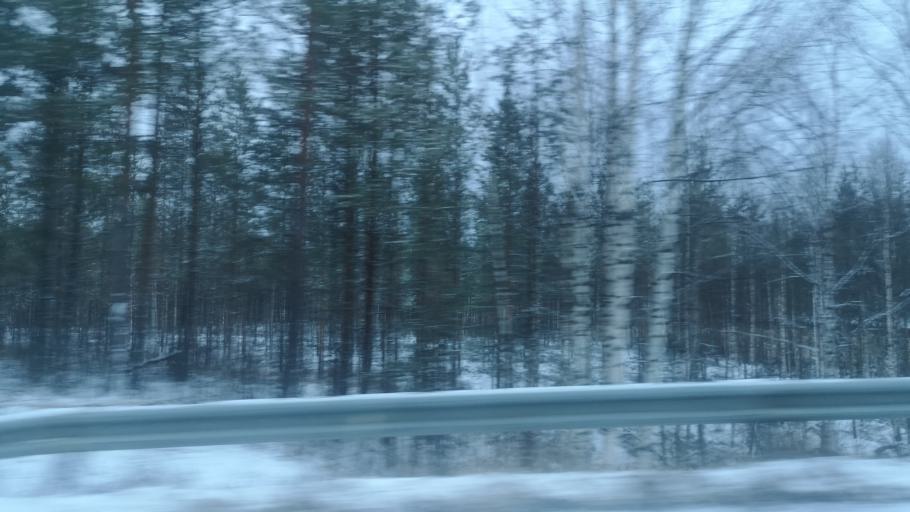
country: FI
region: Southern Savonia
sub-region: Savonlinna
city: Enonkoski
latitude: 62.0992
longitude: 28.6587
